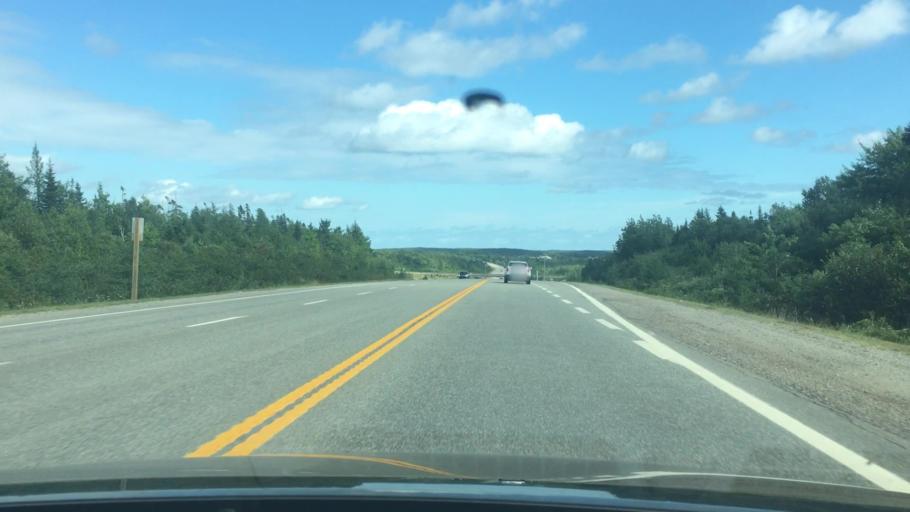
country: CA
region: Nova Scotia
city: Princeville
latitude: 45.6141
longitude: -61.0896
